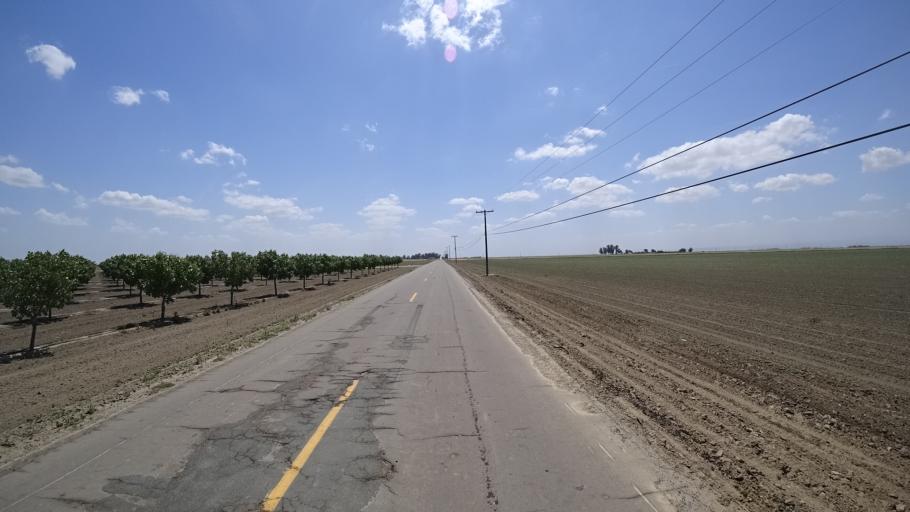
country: US
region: California
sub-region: Kings County
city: Stratford
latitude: 36.1756
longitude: -119.8161
